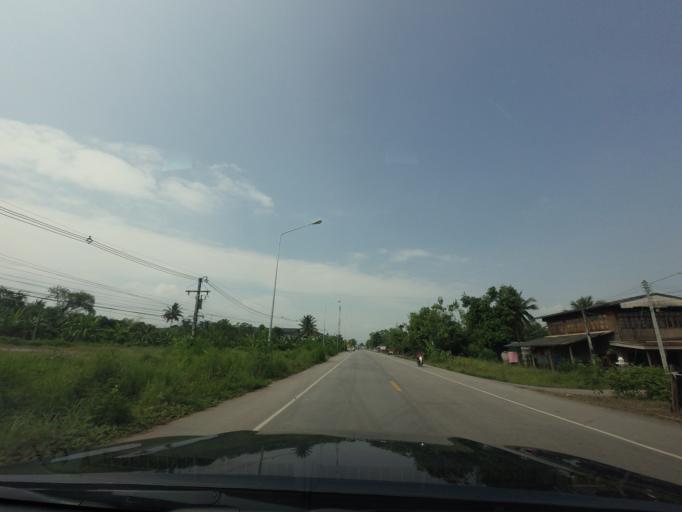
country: LA
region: Xiagnabouli
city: Muang Kenthao
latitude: 17.7054
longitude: 101.4172
